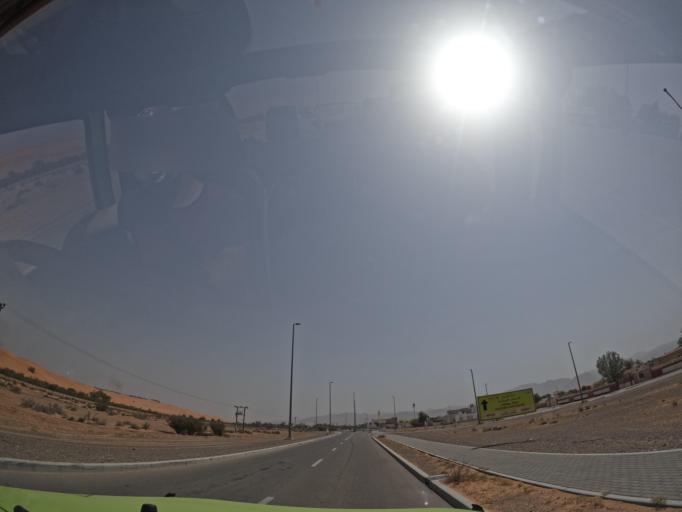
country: OM
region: Al Buraimi
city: Al Buraymi
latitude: 24.7467
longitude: 55.8110
